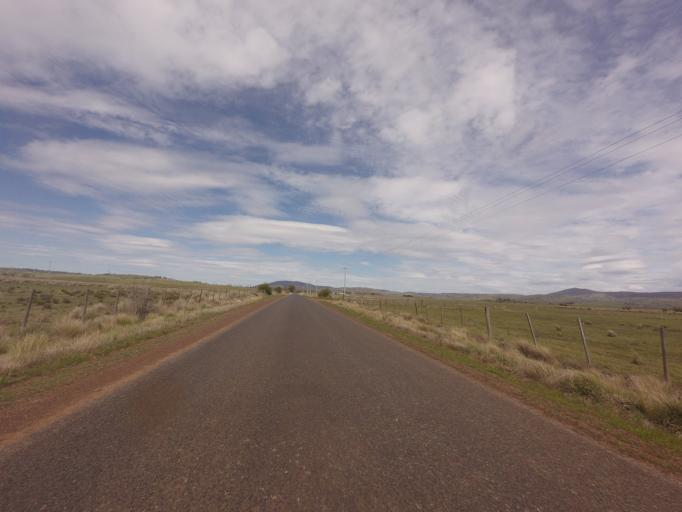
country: AU
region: Tasmania
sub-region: Northern Midlands
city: Evandale
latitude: -41.8680
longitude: 147.3507
